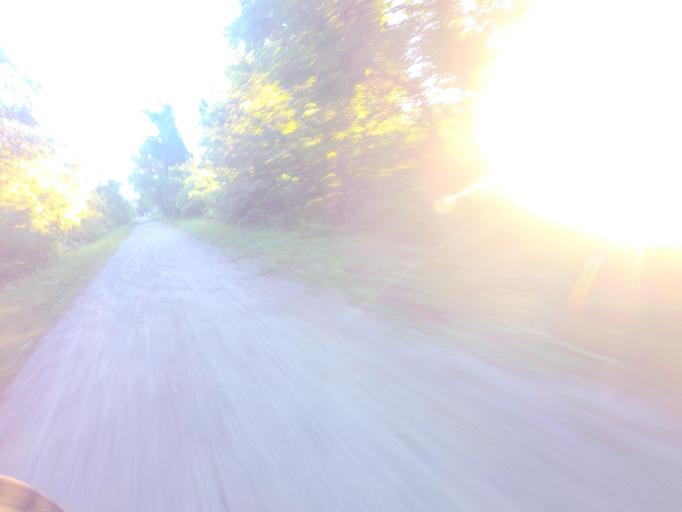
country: CA
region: Ontario
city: Bradford West Gwillimbury
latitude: 43.9957
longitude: -79.8037
